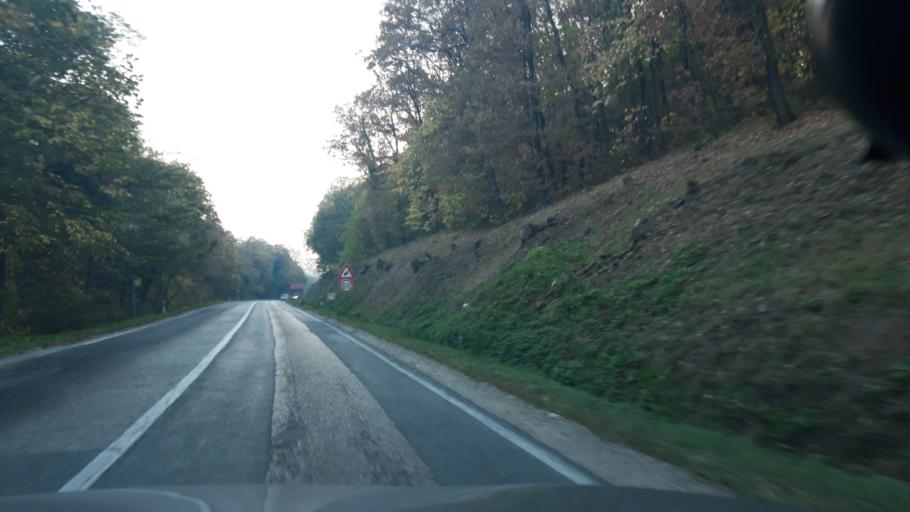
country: RS
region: Autonomna Pokrajina Vojvodina
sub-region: Sremski Okrug
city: Irig
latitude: 45.1411
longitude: 19.8366
